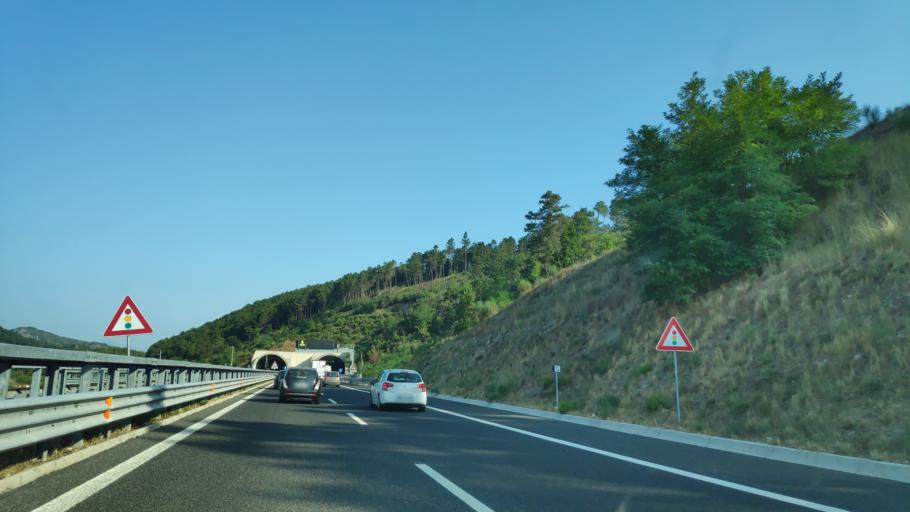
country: IT
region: Campania
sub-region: Provincia di Salerno
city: Casalbuono
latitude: 40.1850
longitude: 15.7097
